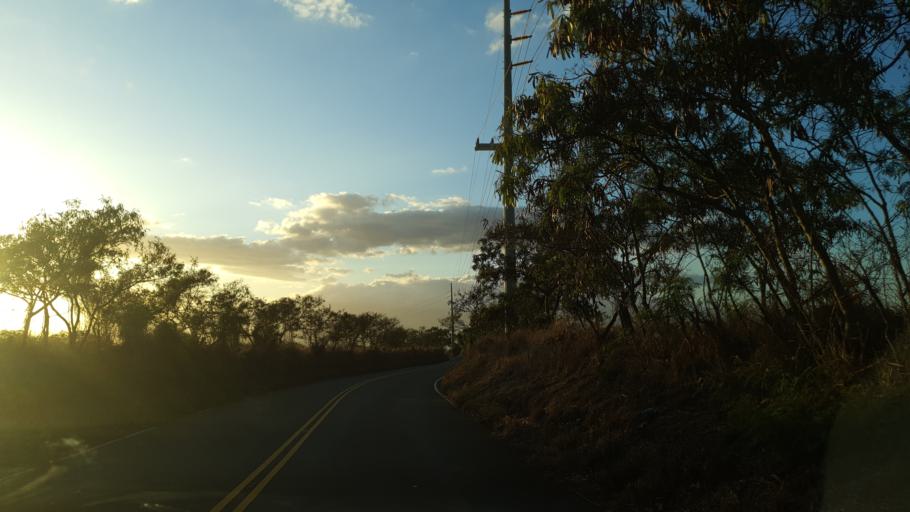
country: US
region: Hawaii
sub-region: Maui County
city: Pukalani
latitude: 20.7909
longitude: -156.3568
